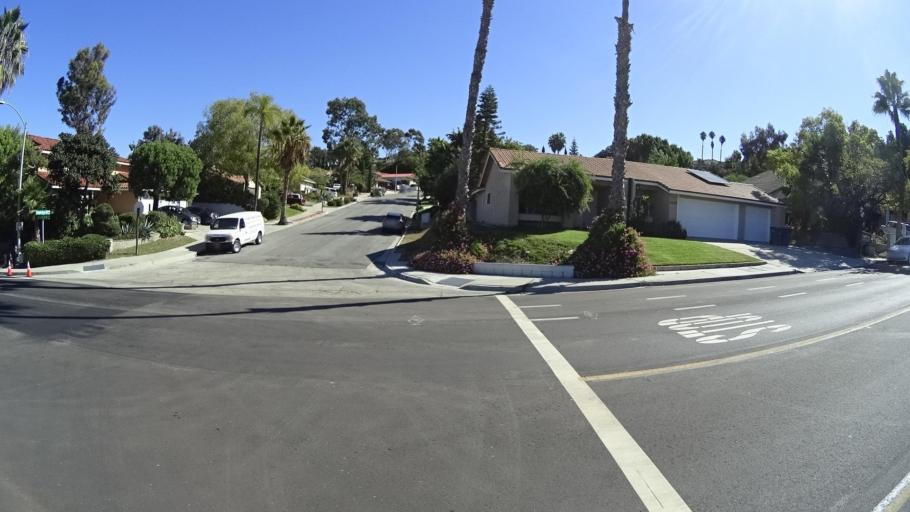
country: US
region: California
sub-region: San Diego County
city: Bonita
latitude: 32.6639
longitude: -117.0013
